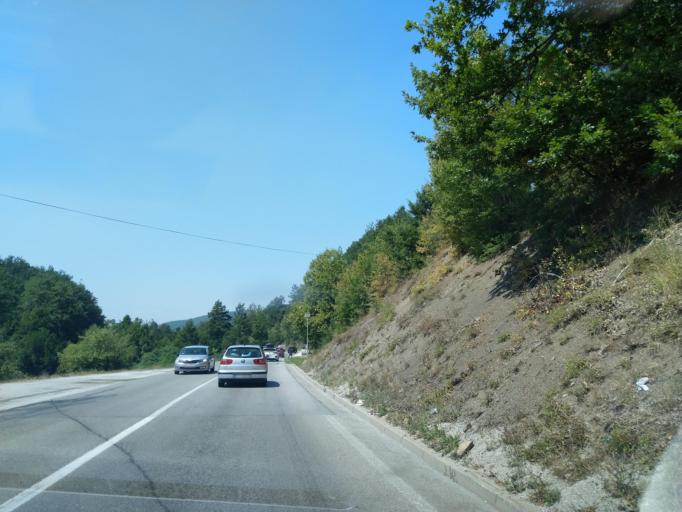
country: RS
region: Central Serbia
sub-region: Zlatiborski Okrug
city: Nova Varos
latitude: 43.4613
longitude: 19.7658
